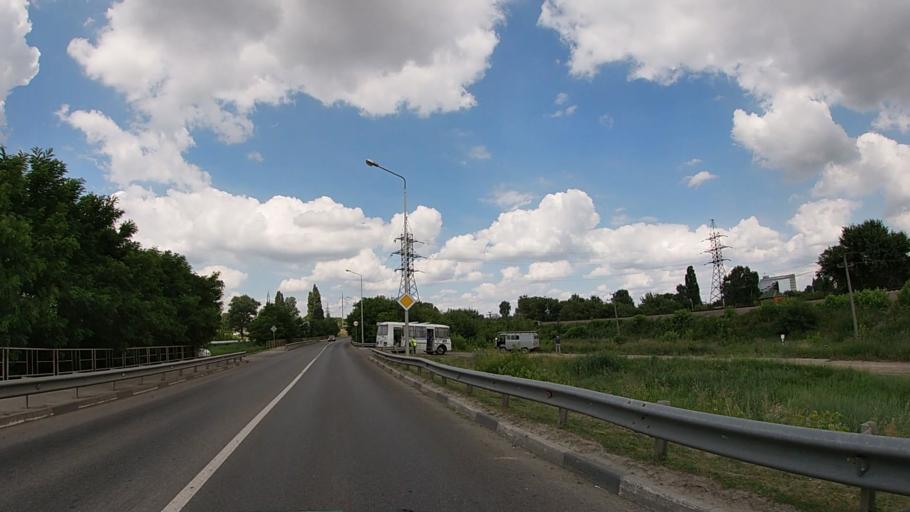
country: RU
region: Belgorod
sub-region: Belgorodskiy Rayon
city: Belgorod
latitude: 50.5918
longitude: 36.5634
